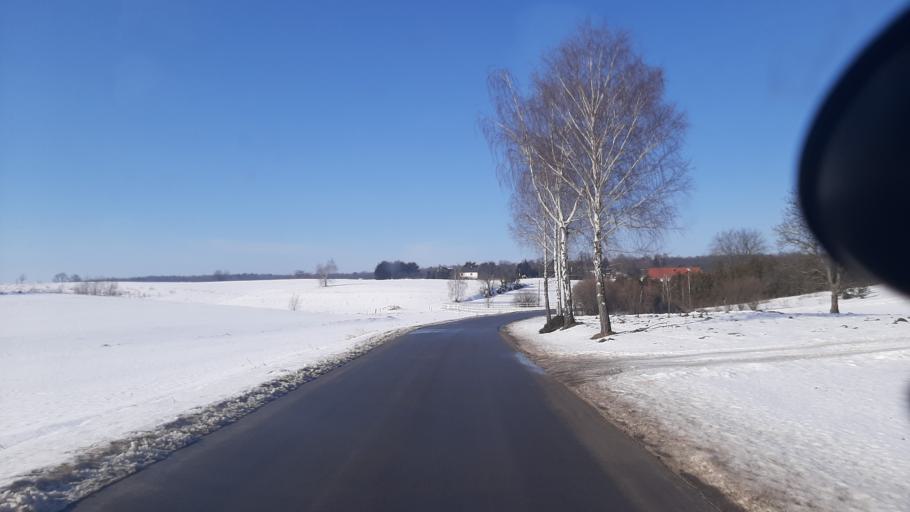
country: PL
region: Lublin Voivodeship
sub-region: Powiat pulawski
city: Naleczow
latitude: 51.2890
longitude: 22.2747
